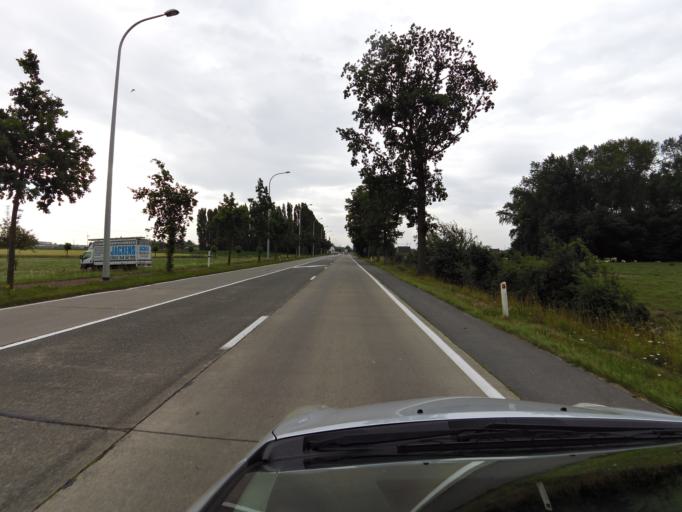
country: BE
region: Flanders
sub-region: Provincie West-Vlaanderen
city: Zuienkerke
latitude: 51.2756
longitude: 3.1738
